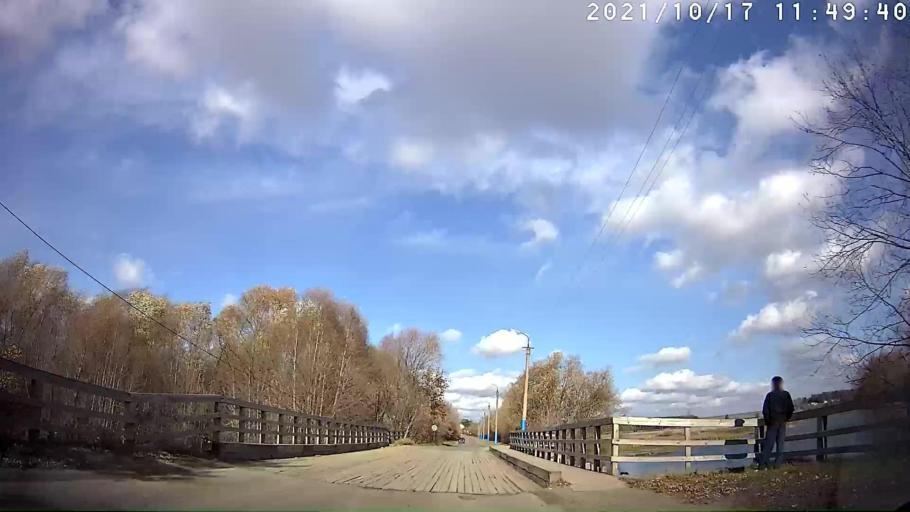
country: RU
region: Mariy-El
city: Kuzhener
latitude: 57.0076
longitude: 48.7368
